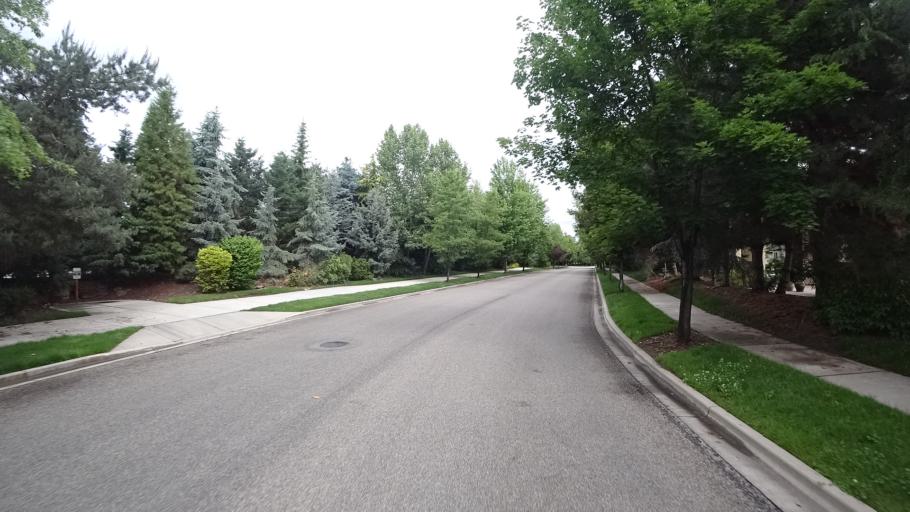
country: US
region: Idaho
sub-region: Ada County
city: Eagle
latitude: 43.6777
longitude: -116.3561
